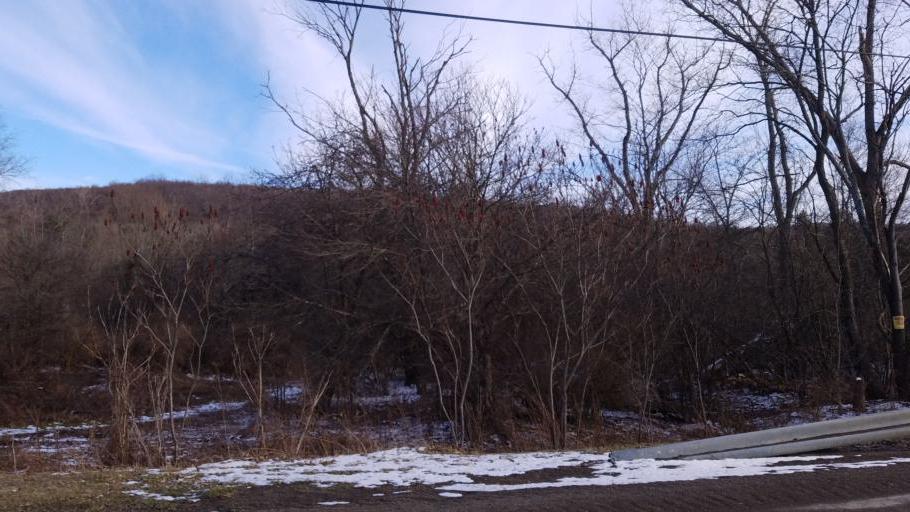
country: US
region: New York
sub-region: Allegany County
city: Wellsville
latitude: 42.1844
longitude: -77.9080
